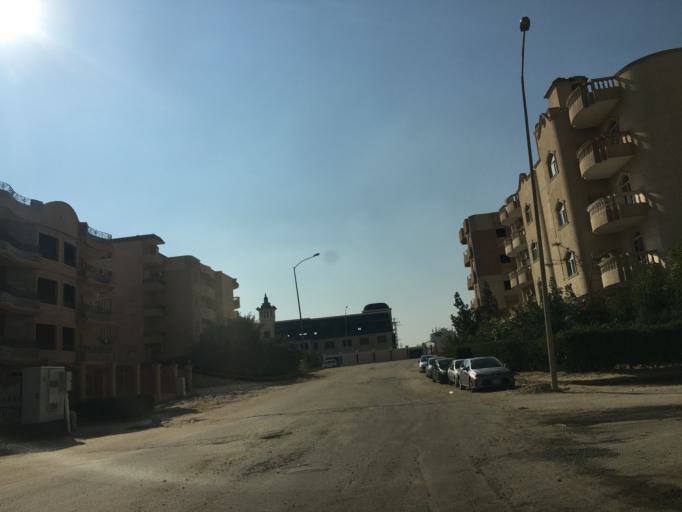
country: EG
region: Al Jizah
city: Madinat Sittah Uktubar
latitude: 29.9963
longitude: 30.9885
